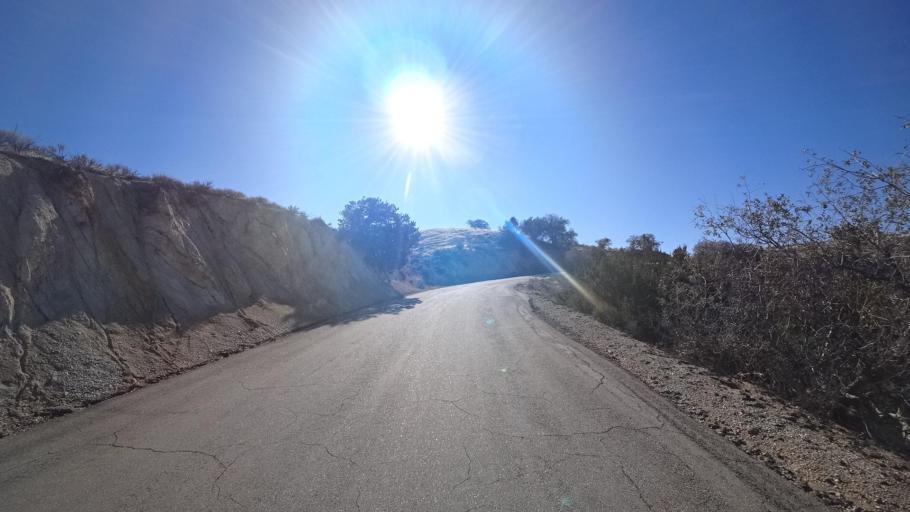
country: US
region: California
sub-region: Kern County
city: Maricopa
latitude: 34.9425
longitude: -119.4040
